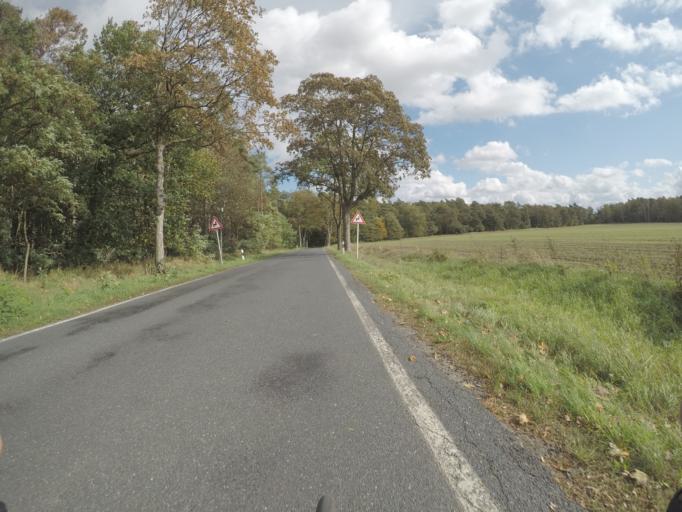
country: DE
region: Brandenburg
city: Strausberg
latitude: 52.6049
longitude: 13.8287
